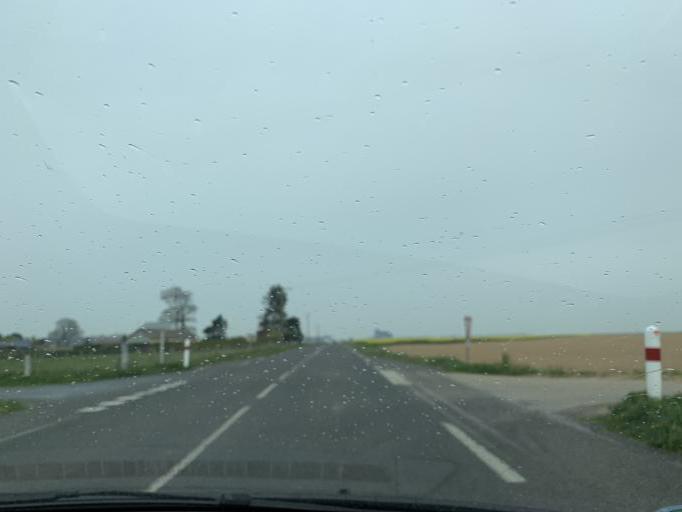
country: FR
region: Haute-Normandie
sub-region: Departement de la Seine-Maritime
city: Cany-Barville
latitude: 49.8098
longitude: 0.6685
